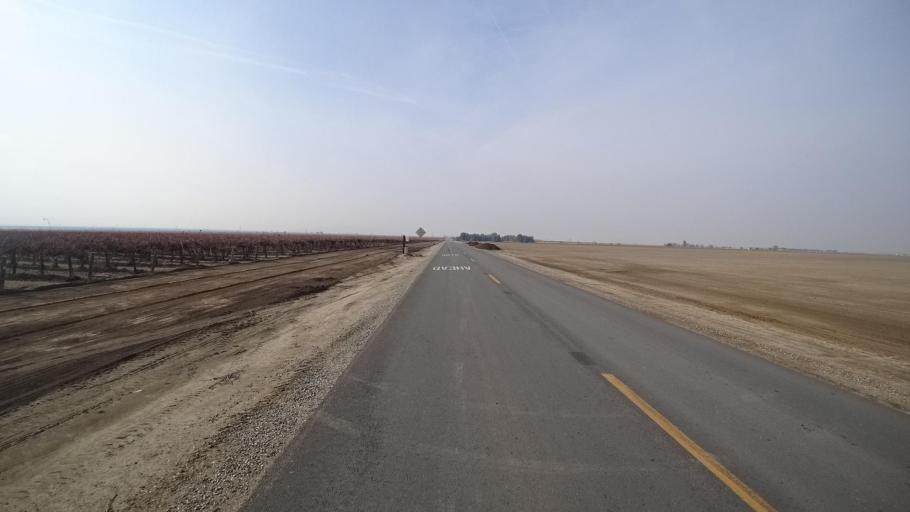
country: US
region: California
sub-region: Kern County
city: Arvin
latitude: 35.0453
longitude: -118.8483
